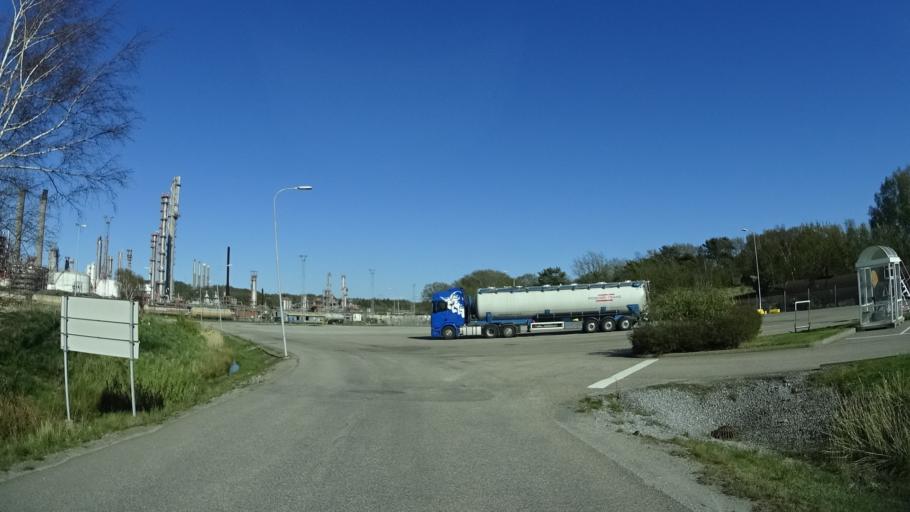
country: SE
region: Vaestra Goetaland
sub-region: Stenungsunds Kommun
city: Stenungsund
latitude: 58.0822
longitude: 11.8183
